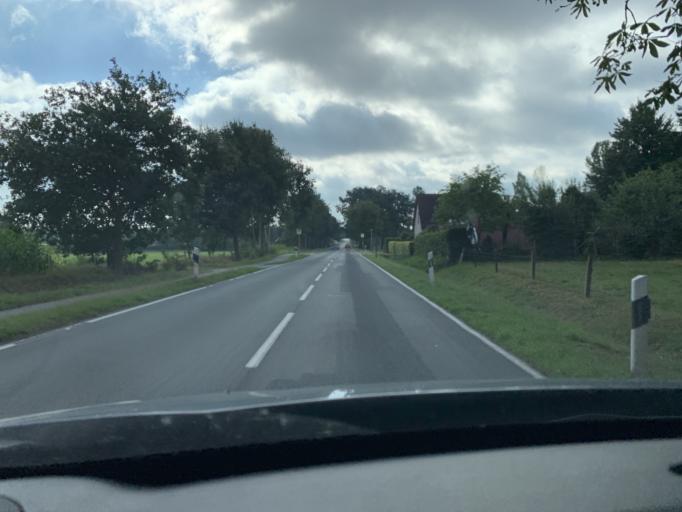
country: DE
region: Lower Saxony
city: Wardenburg
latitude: 53.0898
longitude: 8.1097
